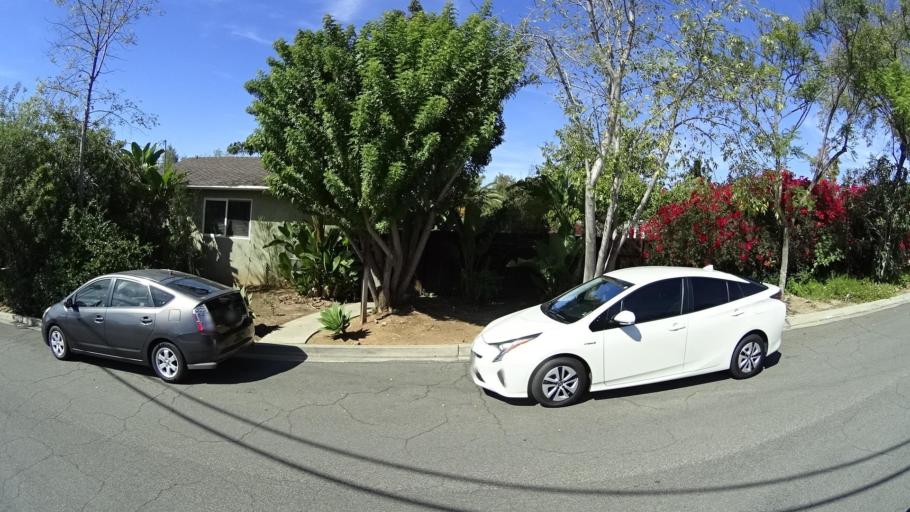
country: US
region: California
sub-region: San Diego County
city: Casa de Oro-Mount Helix
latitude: 32.7565
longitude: -116.9551
